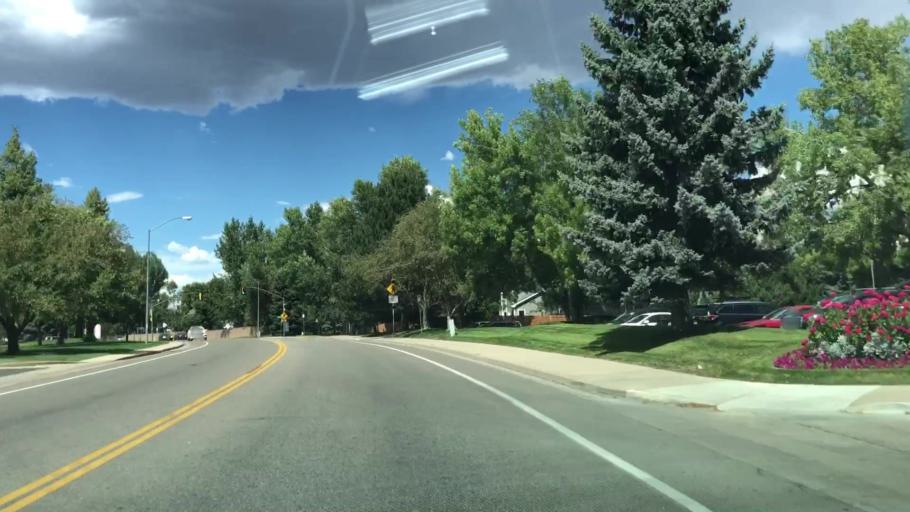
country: US
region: Colorado
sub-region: Larimer County
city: Fort Collins
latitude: 40.5268
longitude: -105.0664
